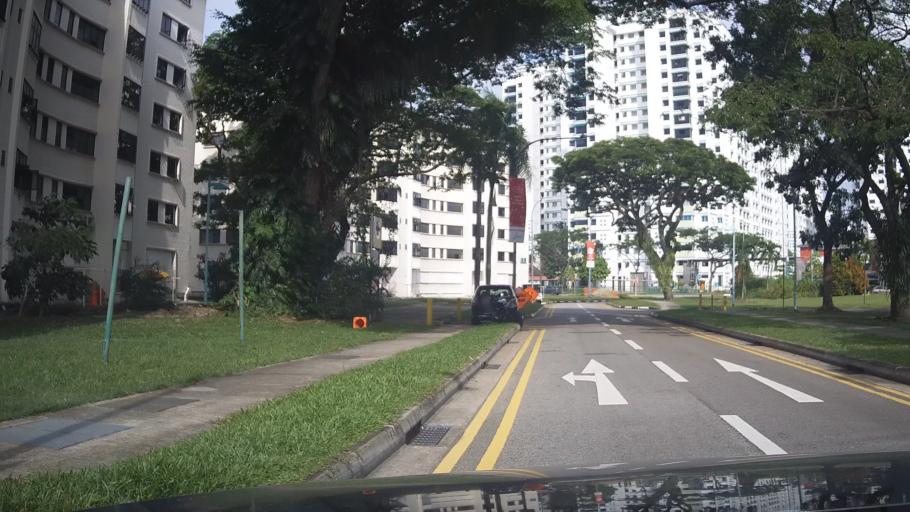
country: SG
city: Singapore
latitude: 1.3058
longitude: 103.8843
